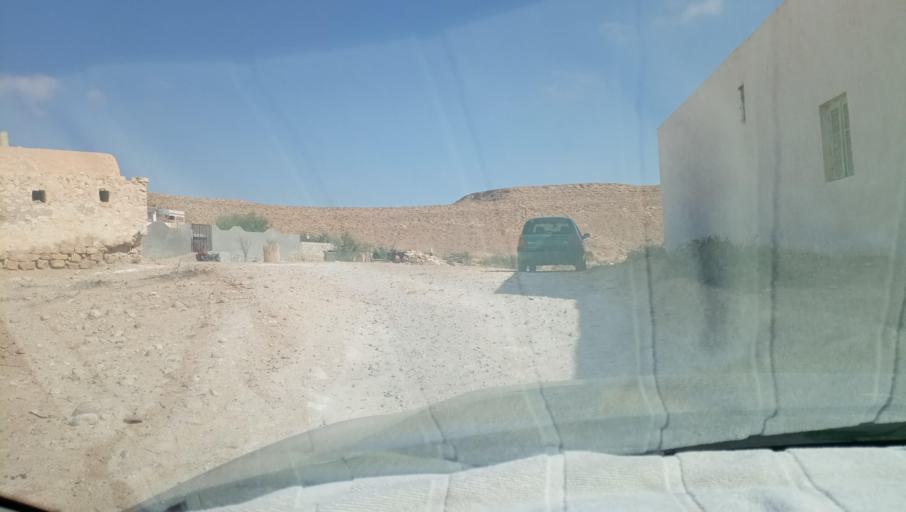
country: TN
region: Tataouine
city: Tataouine
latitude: 32.9851
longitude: 10.3857
